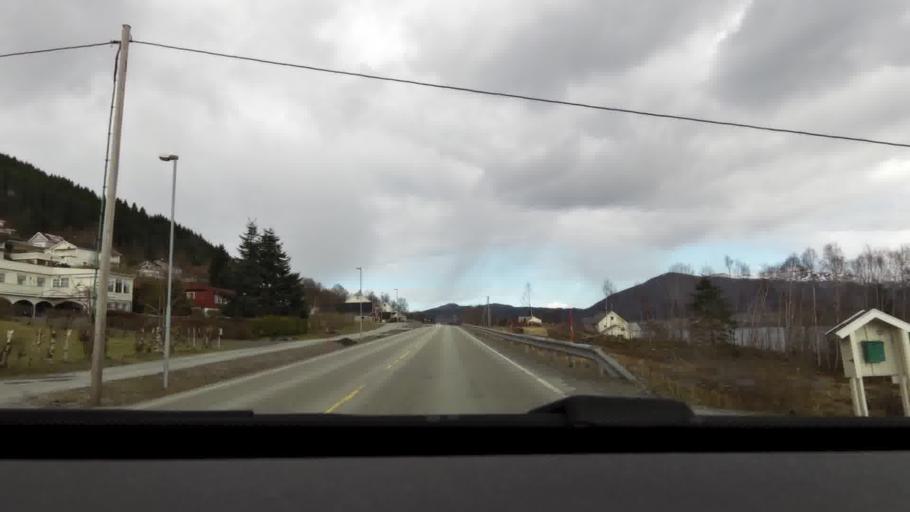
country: NO
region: More og Romsdal
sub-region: Eide
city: Eide
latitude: 62.9245
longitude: 7.4473
